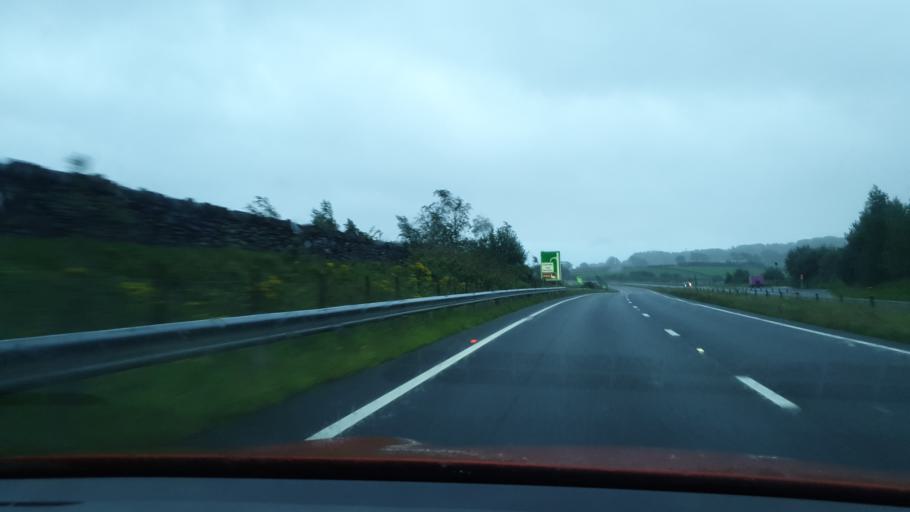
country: GB
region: England
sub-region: Cumbria
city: Grange-over-Sands
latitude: 54.2320
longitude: -2.9153
